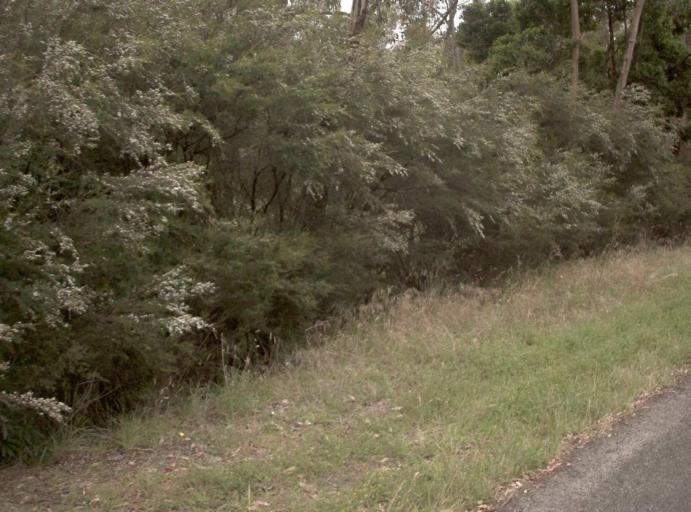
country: AU
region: Victoria
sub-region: Wellington
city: Sale
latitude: -38.5256
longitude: 146.8718
